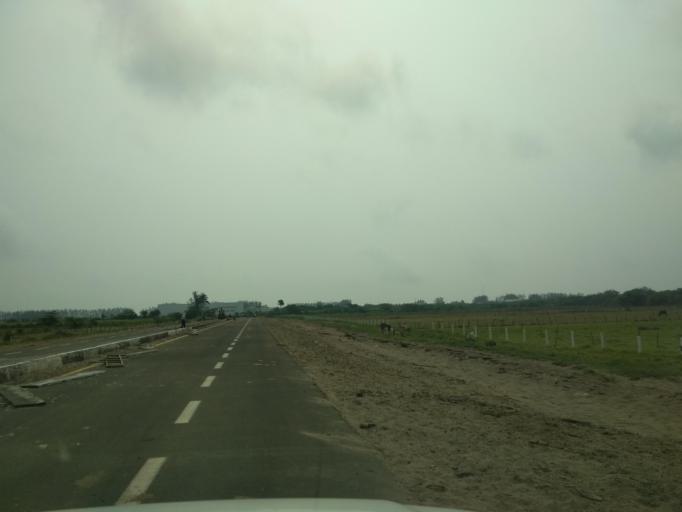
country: MX
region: Veracruz
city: Anton Lizardo
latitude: 19.0454
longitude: -95.9827
